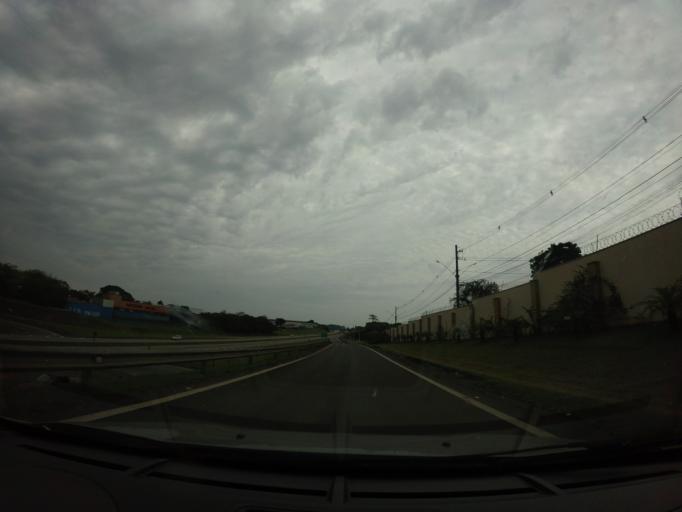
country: BR
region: Sao Paulo
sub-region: Piracicaba
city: Piracicaba
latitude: -22.7352
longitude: -47.6016
